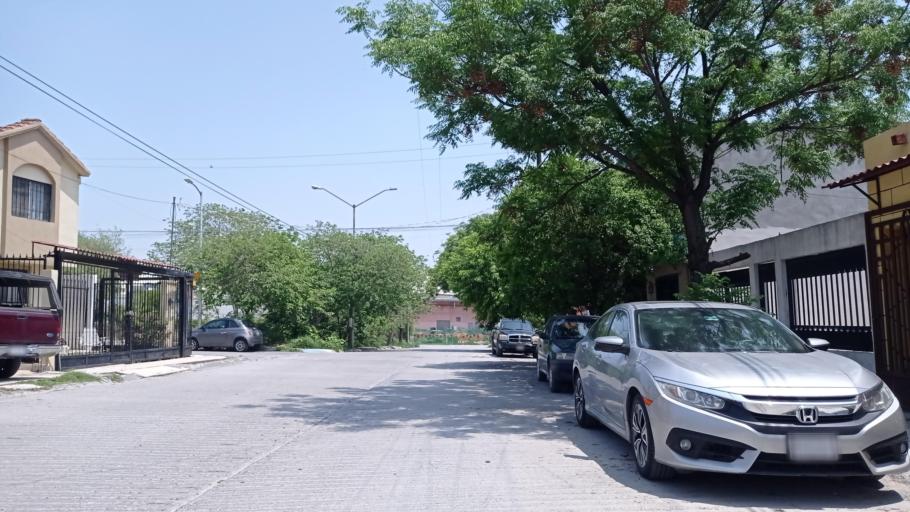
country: MX
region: Nuevo Leon
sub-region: Juarez
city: Jardines de la Silla (Jardines)
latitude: 25.6547
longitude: -100.1895
